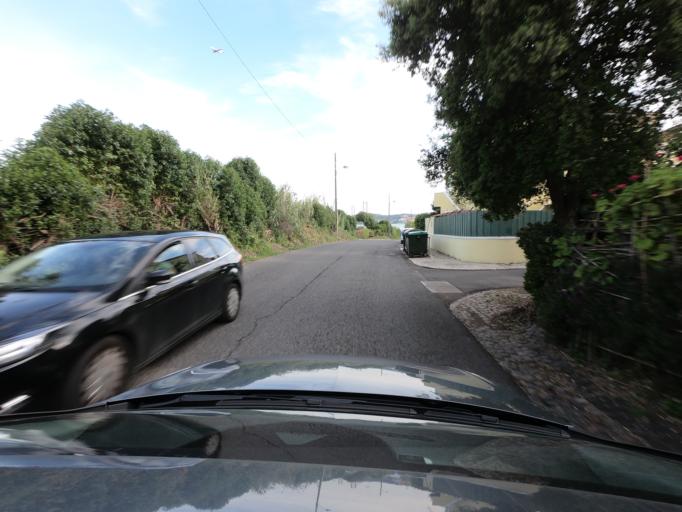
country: PT
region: Setubal
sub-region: Almada
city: Pragal
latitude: 38.7152
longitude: -9.1796
